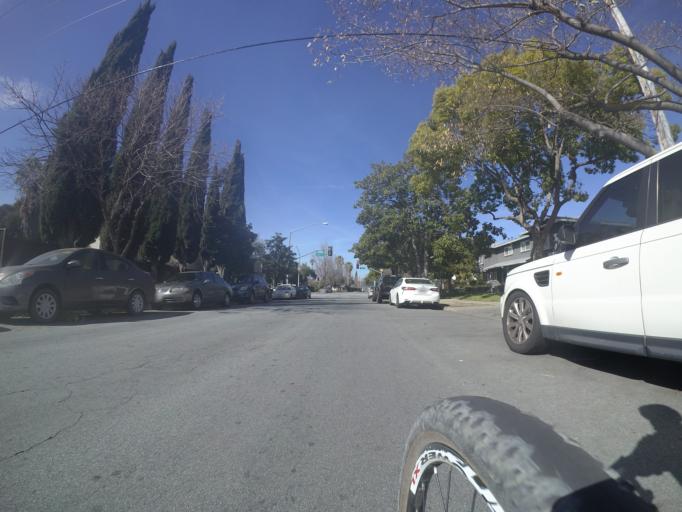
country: US
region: California
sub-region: Santa Clara County
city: Milpitas
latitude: 37.4186
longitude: -121.8673
